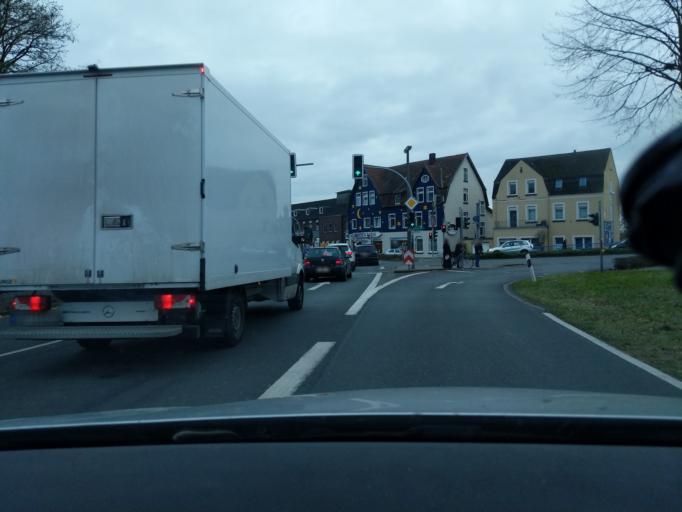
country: DE
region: North Rhine-Westphalia
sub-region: Regierungsbezirk Munster
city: Greven
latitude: 52.0946
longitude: 7.6042
